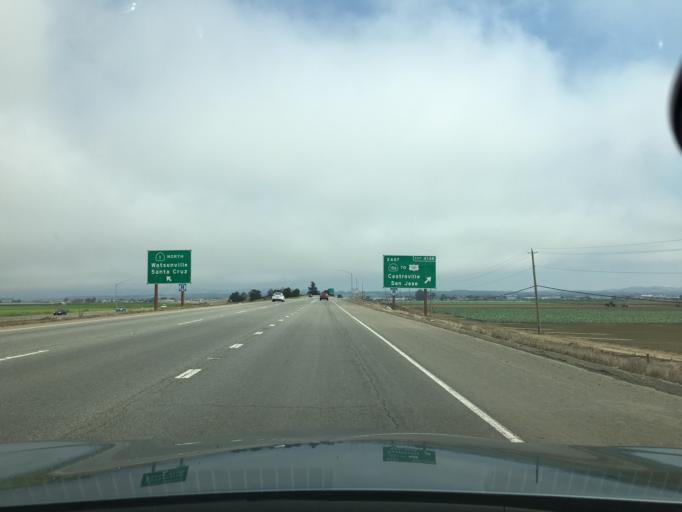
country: US
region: California
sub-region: Monterey County
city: Castroville
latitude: 36.7477
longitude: -121.7696
